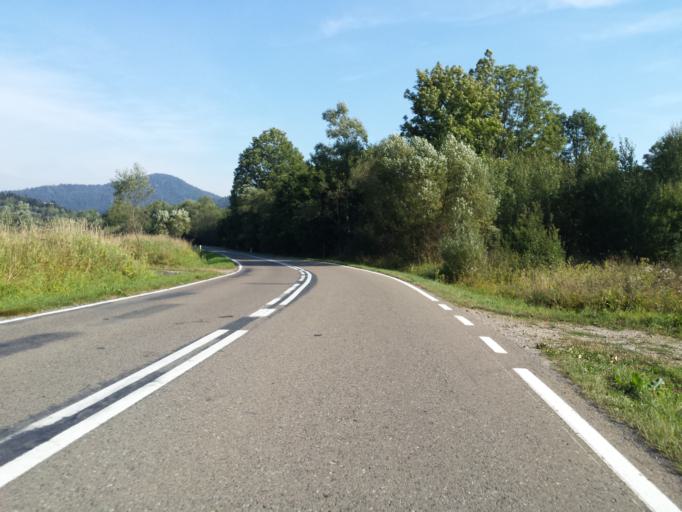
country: PL
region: Subcarpathian Voivodeship
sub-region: Powiat leski
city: Cisna
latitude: 49.2603
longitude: 22.2884
